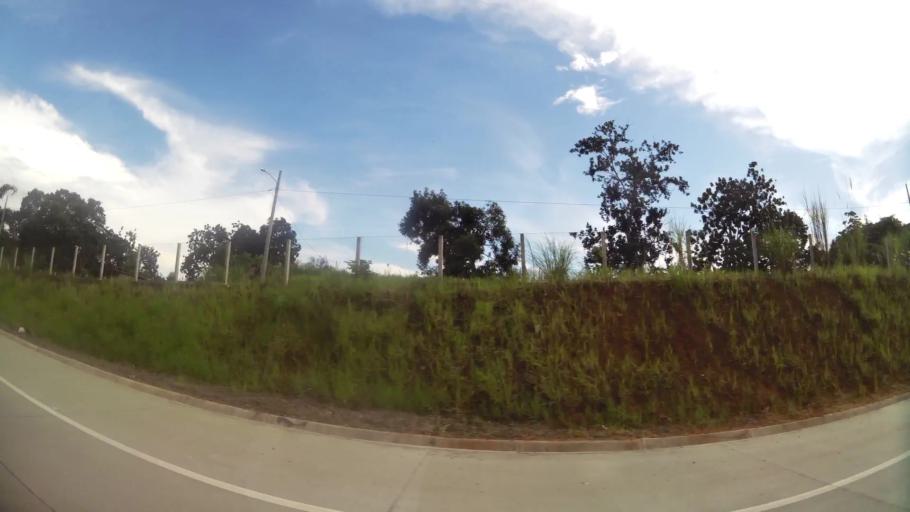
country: PA
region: Panama
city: San Miguelito
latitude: 9.0840
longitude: -79.4453
